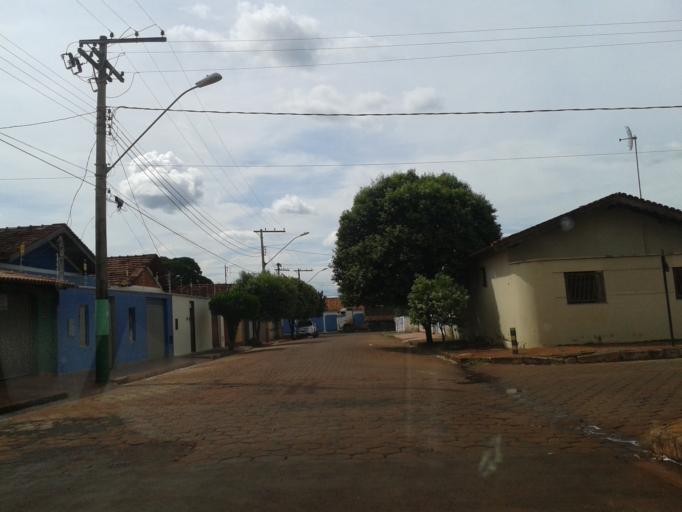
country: BR
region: Minas Gerais
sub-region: Centralina
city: Centralina
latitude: -18.5873
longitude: -49.2003
